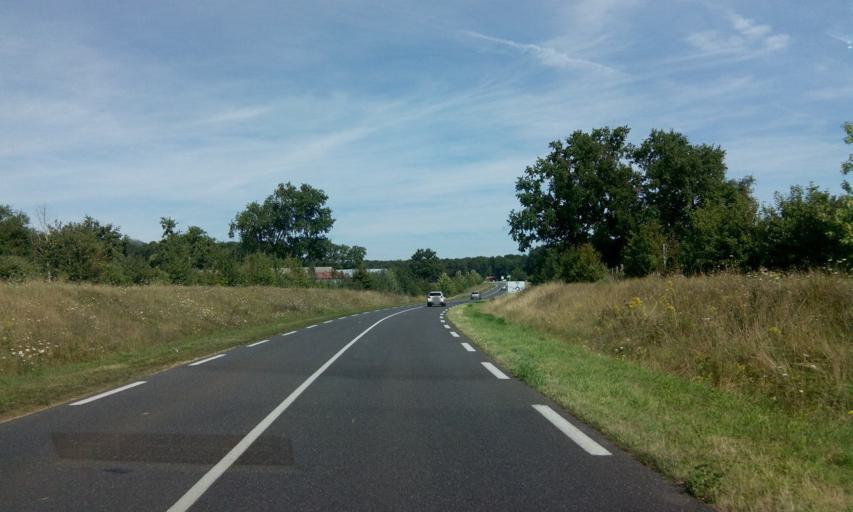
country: FR
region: Poitou-Charentes
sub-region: Departement de la Vienne
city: Availles-Limouzine
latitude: 46.1101
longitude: 0.5668
